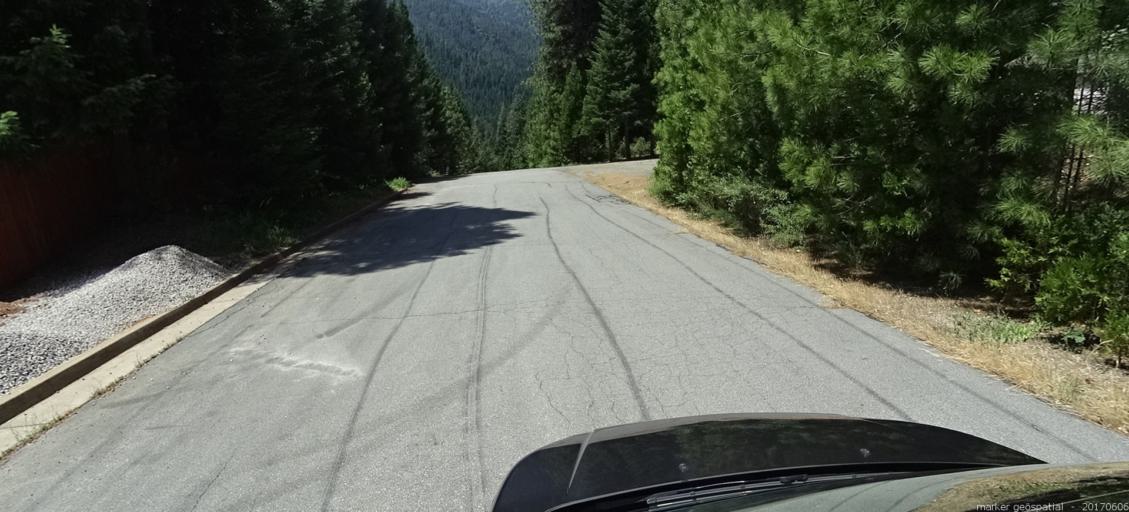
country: US
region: California
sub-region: Siskiyou County
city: Dunsmuir
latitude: 41.2312
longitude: -122.2711
